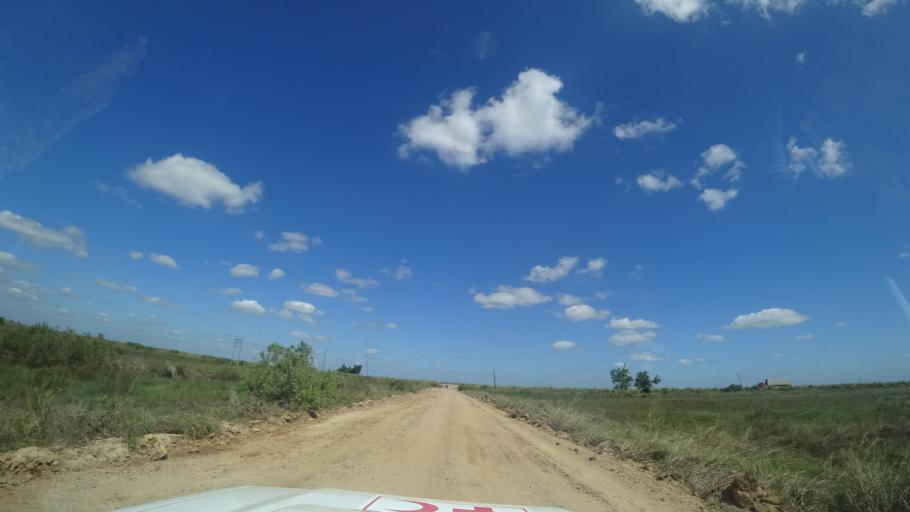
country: MZ
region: Sofala
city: Dondo
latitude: -19.4647
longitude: 34.5608
